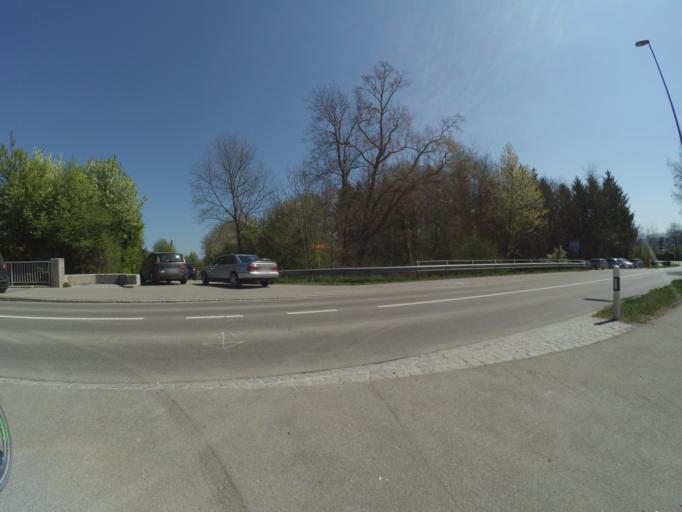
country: CH
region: Thurgau
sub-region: Frauenfeld District
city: Gachnang
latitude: 47.5777
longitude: 8.8341
